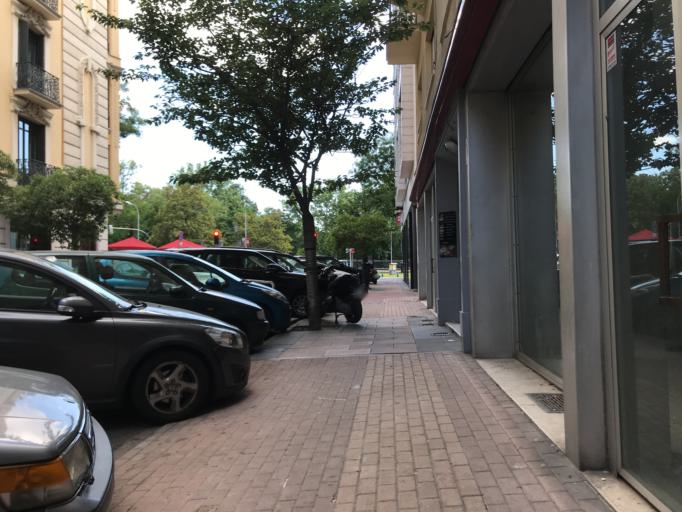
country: ES
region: Madrid
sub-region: Provincia de Madrid
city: Salamanca
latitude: 40.4221
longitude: -3.6829
